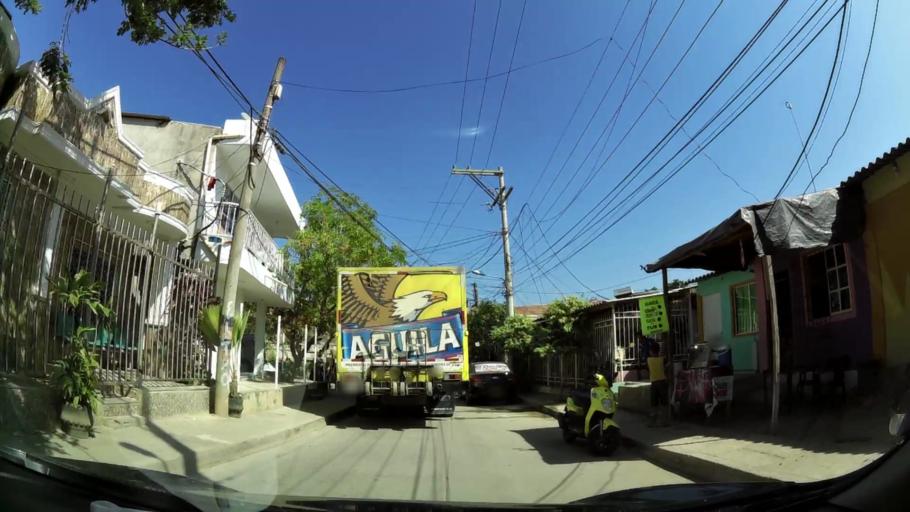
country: CO
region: Bolivar
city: Cartagena
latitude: 10.3713
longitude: -75.4970
